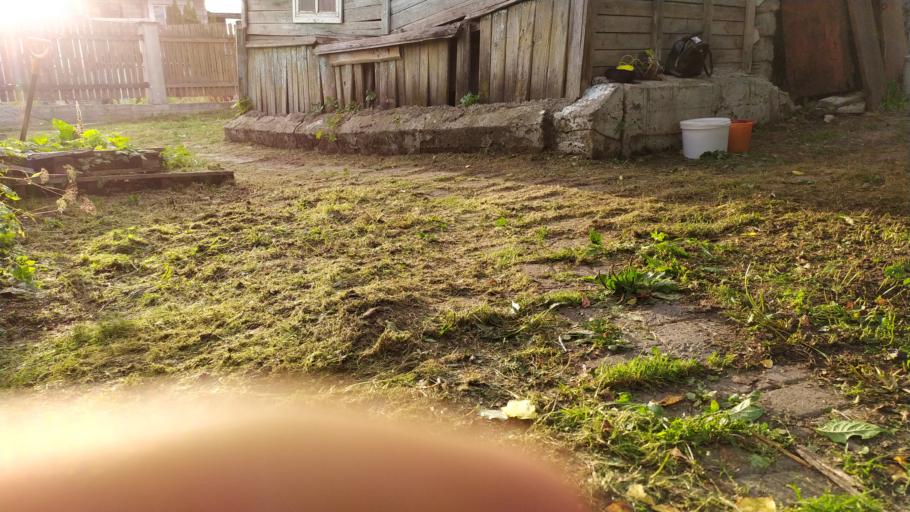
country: RU
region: Leningrad
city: Kirovsk
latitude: 59.8786
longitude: 30.9982
